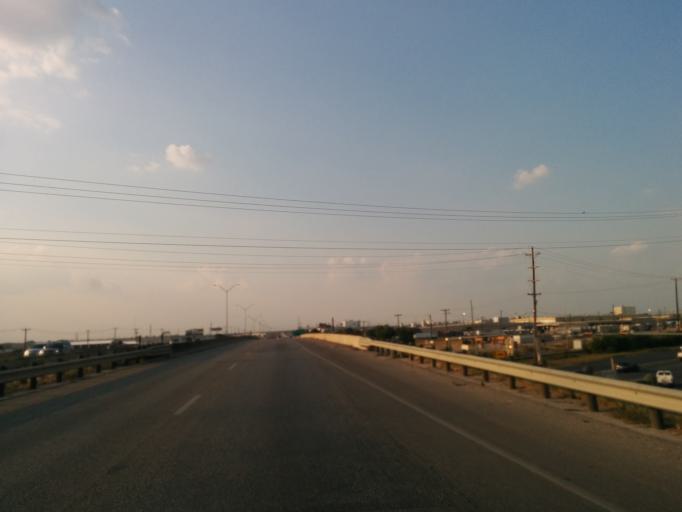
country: US
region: Texas
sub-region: Bexar County
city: Kirby
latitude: 29.4593
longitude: -98.4041
